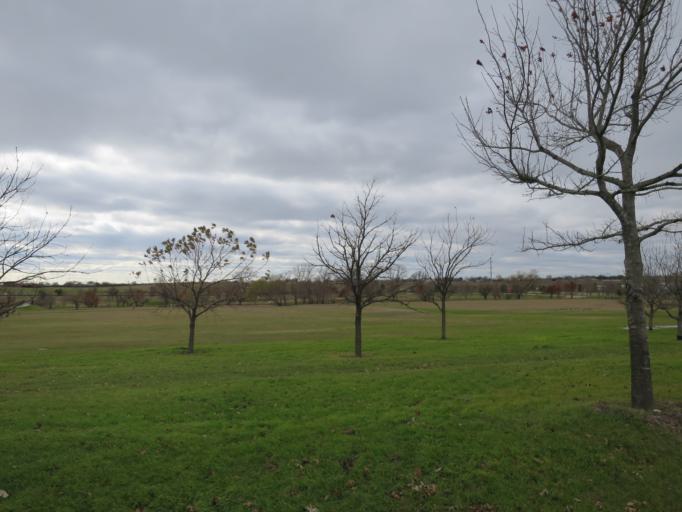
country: US
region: Texas
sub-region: Williamson County
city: Round Rock
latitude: 30.5427
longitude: -97.6259
